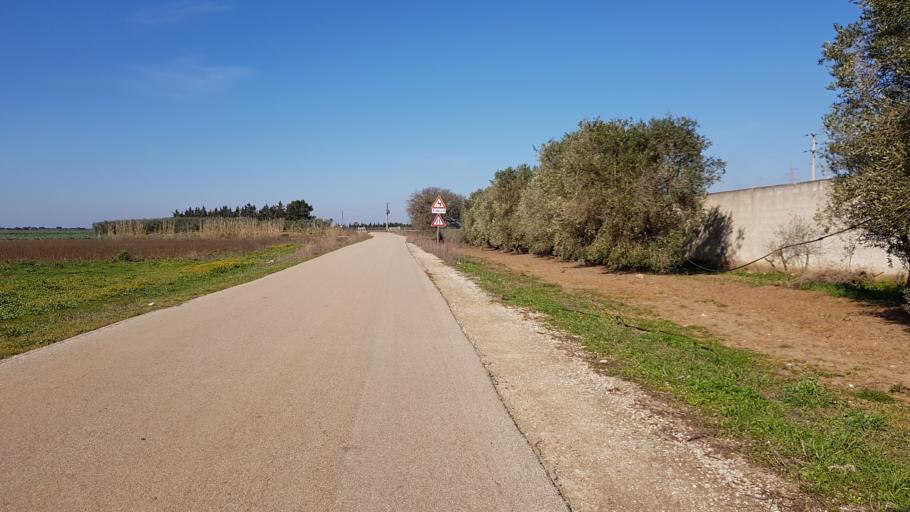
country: IT
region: Apulia
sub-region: Provincia di Brindisi
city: Mesagne
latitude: 40.6190
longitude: 17.8161
